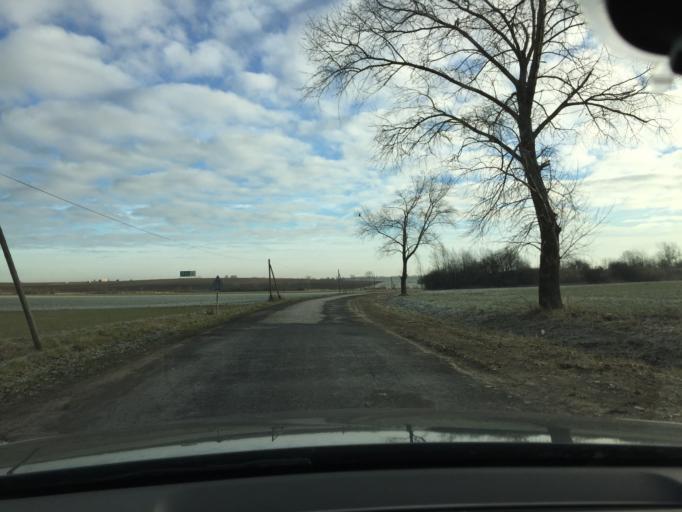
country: PL
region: Lower Silesian Voivodeship
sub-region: Powiat sredzki
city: Udanin
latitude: 51.0638
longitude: 16.4724
